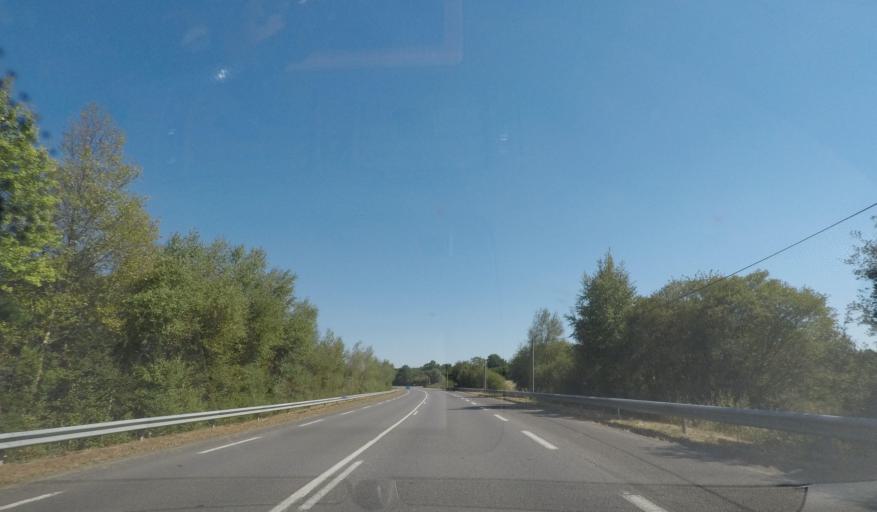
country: FR
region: Brittany
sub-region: Departement du Morbihan
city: Limerzel
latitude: 47.6185
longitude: -2.4037
